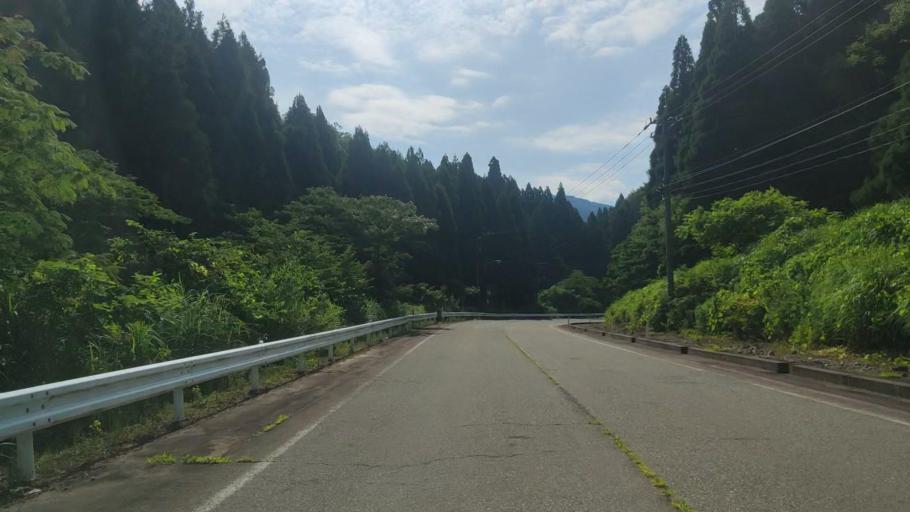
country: JP
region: Ishikawa
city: Komatsu
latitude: 36.3231
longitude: 136.5313
